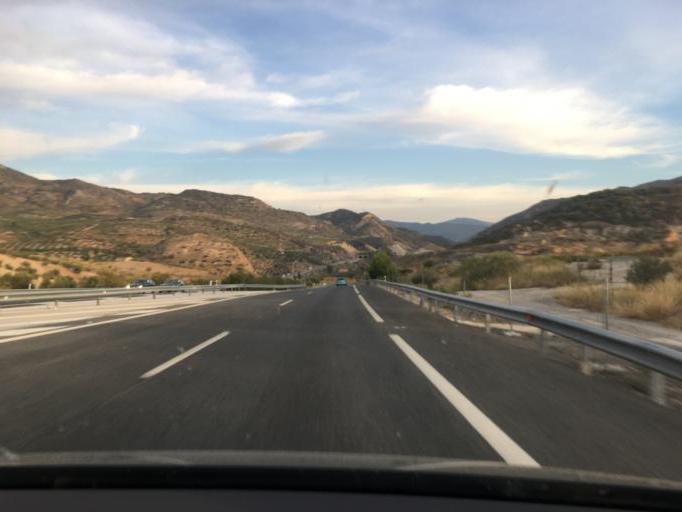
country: ES
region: Andalusia
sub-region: Provincia de Jaen
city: Pegalajar
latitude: 37.7171
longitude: -3.6486
